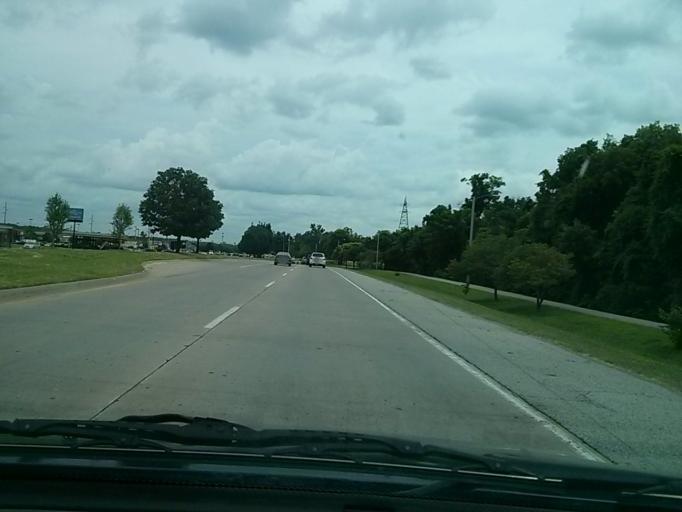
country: US
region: Oklahoma
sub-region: Tulsa County
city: Jenks
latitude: 36.0283
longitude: -95.9520
